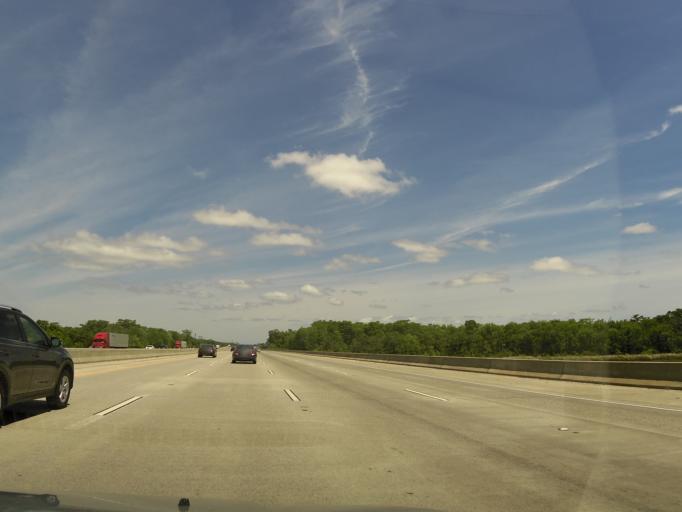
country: US
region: Georgia
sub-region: McIntosh County
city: Darien
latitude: 31.3638
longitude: -81.4575
